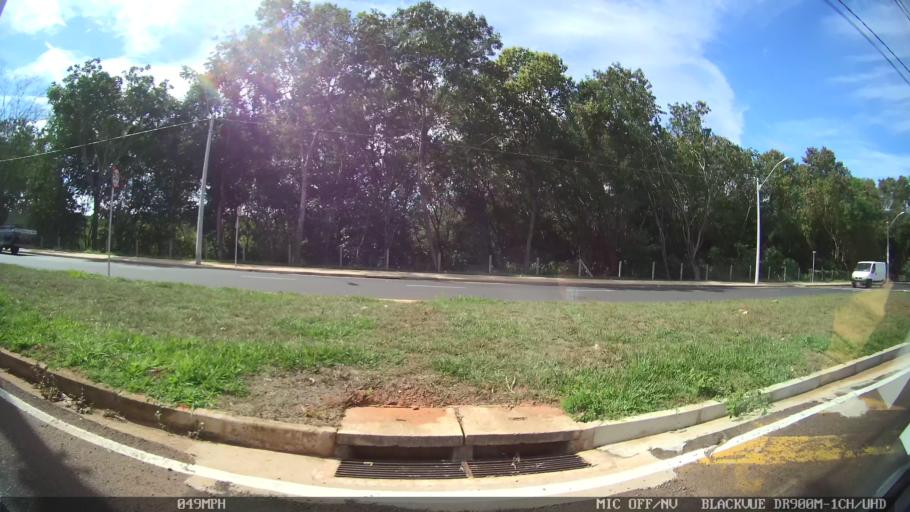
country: BR
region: Sao Paulo
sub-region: Sao Jose Do Rio Preto
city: Sao Jose do Rio Preto
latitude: -20.8372
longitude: -49.3454
